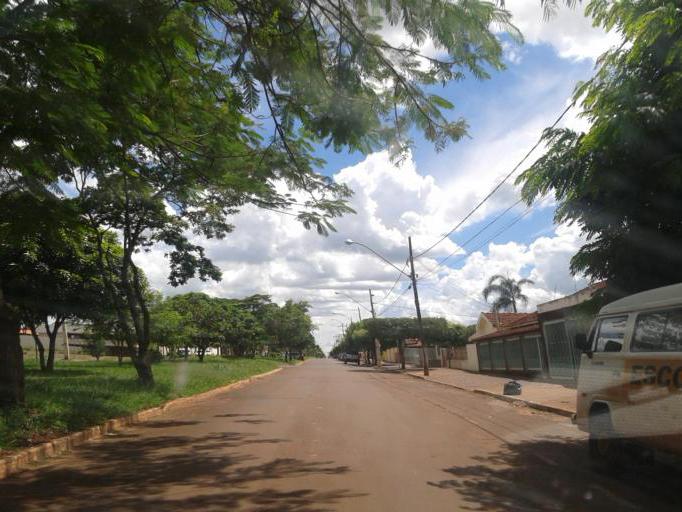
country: BR
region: Minas Gerais
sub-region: Santa Vitoria
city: Santa Vitoria
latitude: -18.8369
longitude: -50.1217
